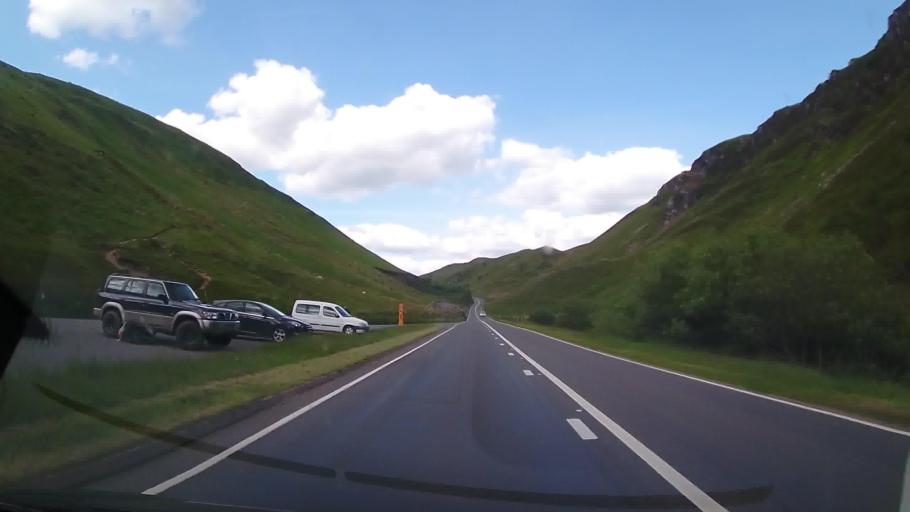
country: GB
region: Wales
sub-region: Gwynedd
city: Corris
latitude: 52.7051
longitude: -3.8472
